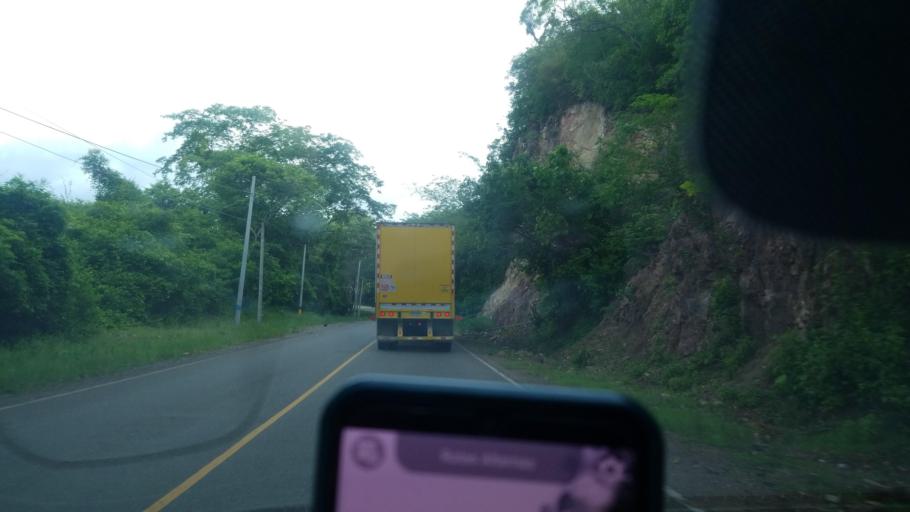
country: HN
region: Santa Barbara
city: Ilama
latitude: 15.0755
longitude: -88.2253
